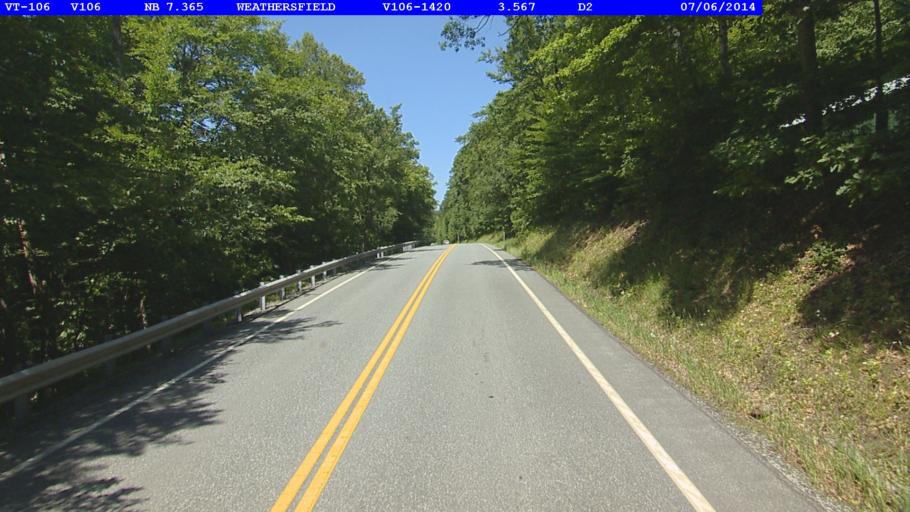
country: US
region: Vermont
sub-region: Windsor County
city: Springfield
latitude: 43.3899
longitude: -72.5138
